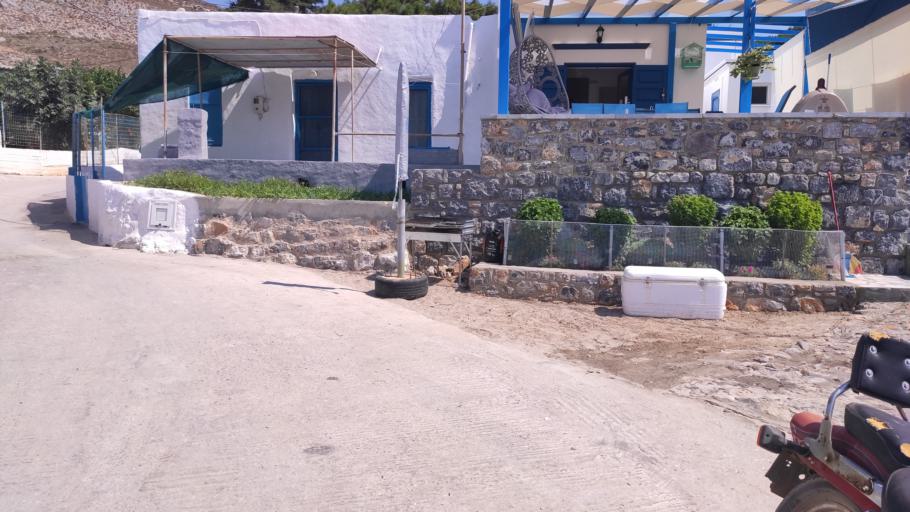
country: GR
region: South Aegean
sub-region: Nomos Dodekanisou
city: Pylion
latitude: 36.9333
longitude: 27.1324
